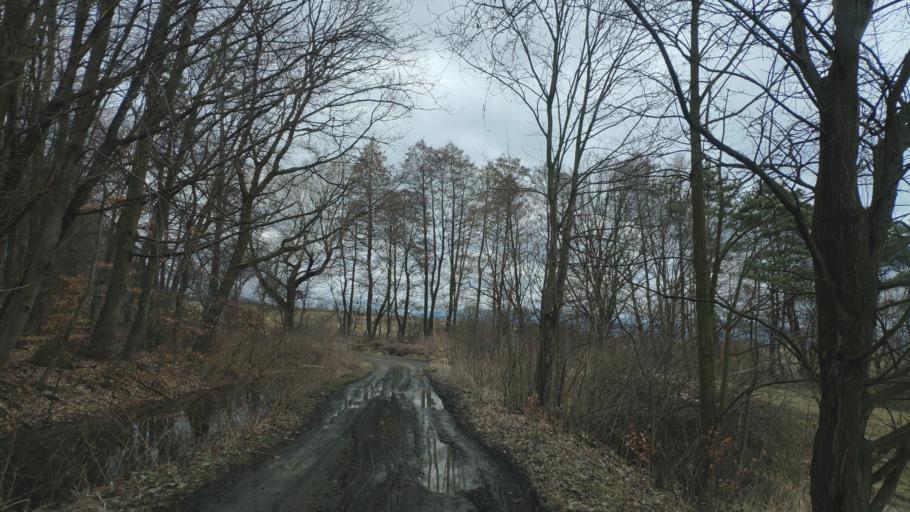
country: SK
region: Presovsky
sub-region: Okres Presov
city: Presov
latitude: 49.0759
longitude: 21.2713
